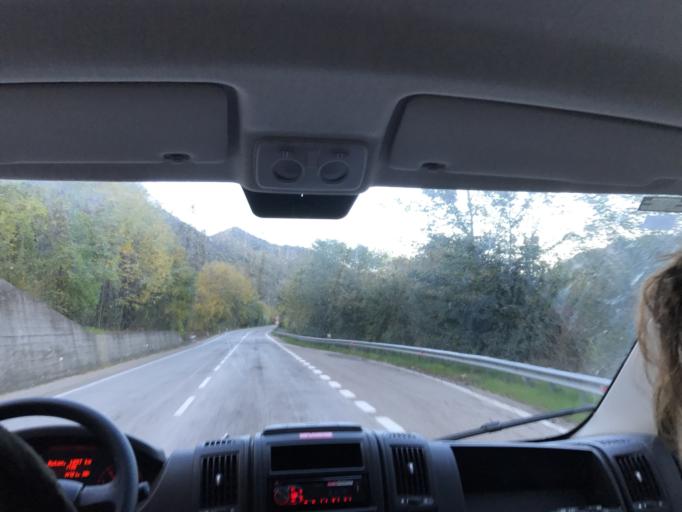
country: IT
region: The Marches
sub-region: Provincia di Ascoli Piceno
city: Marsia
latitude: 42.8181
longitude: 13.5039
